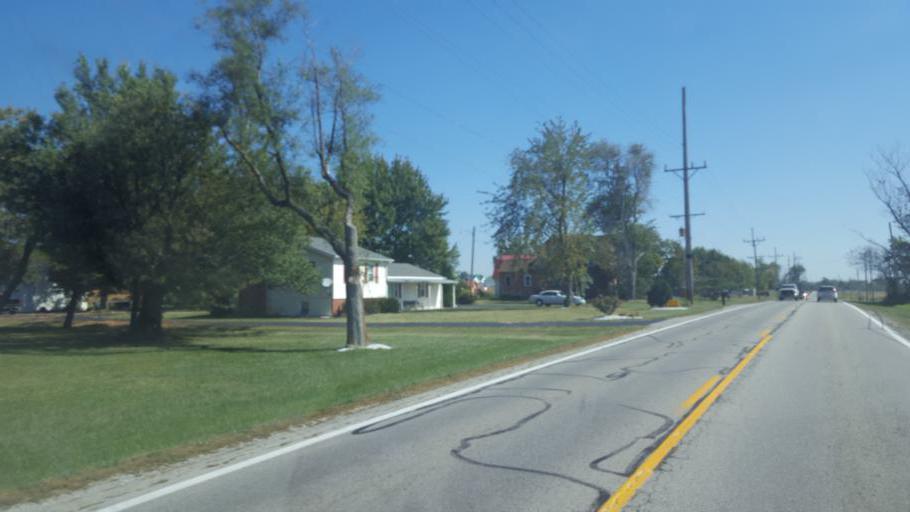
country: US
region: Ohio
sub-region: Marion County
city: Marion
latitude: 40.6123
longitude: -83.2072
